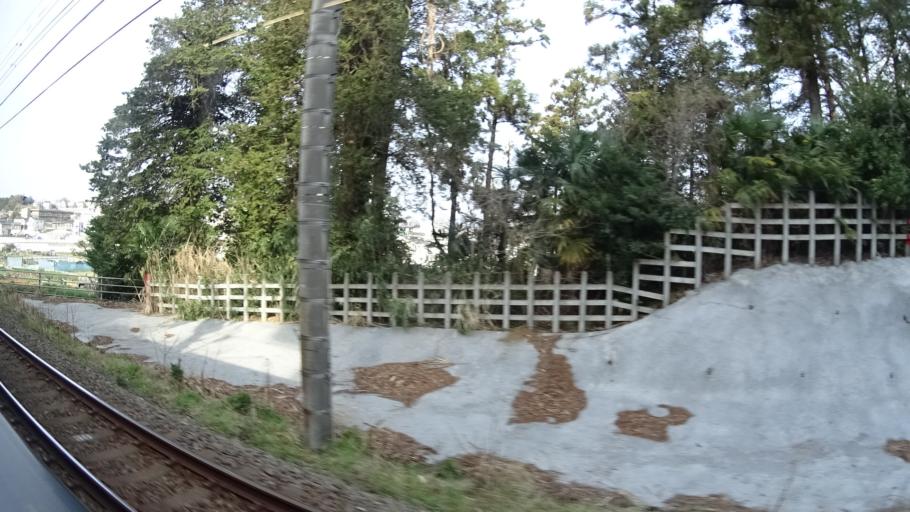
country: JP
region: Kanagawa
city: Zama
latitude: 35.4611
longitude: 139.4081
